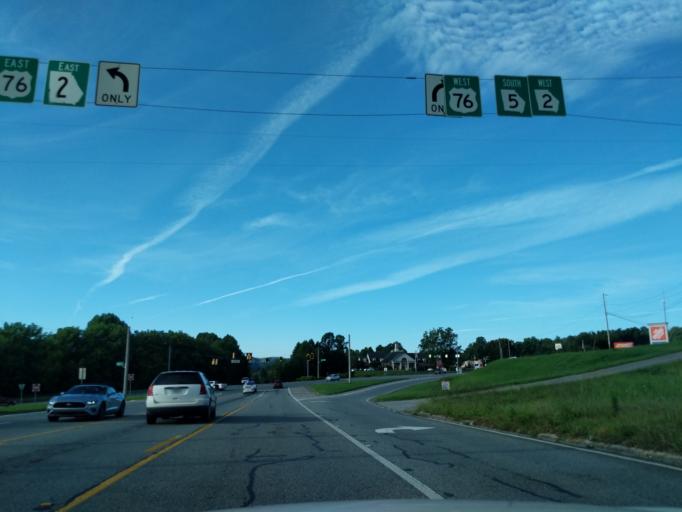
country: US
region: Georgia
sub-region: Fannin County
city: Blue Ridge
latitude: 34.8742
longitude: -84.3225
